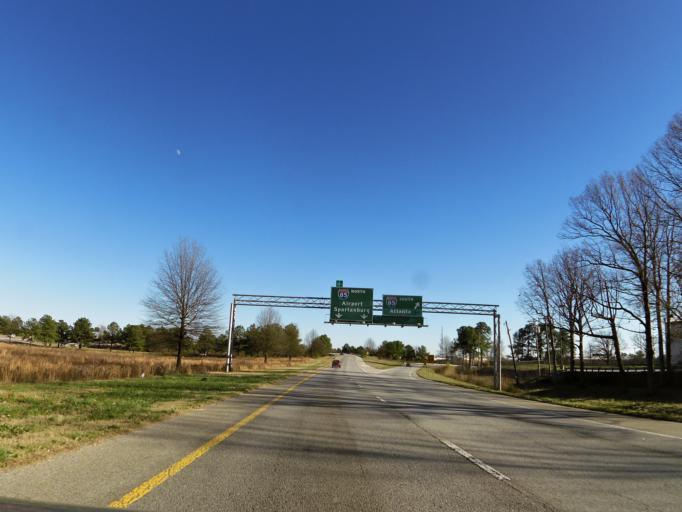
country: US
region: South Carolina
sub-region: Greenville County
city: Mauldin
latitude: 34.8340
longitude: -82.3022
